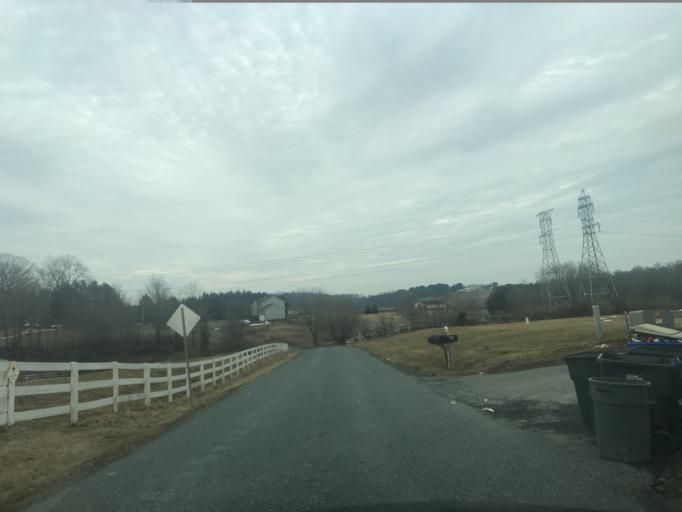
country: US
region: Maryland
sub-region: Harford County
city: Jarrettsville
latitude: 39.6786
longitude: -76.4240
